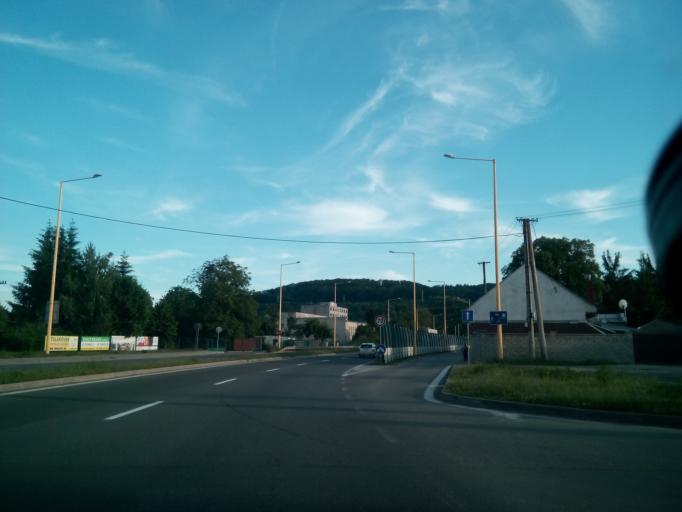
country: SK
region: Presovsky
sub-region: Okres Presov
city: Presov
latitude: 48.9932
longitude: 21.2303
